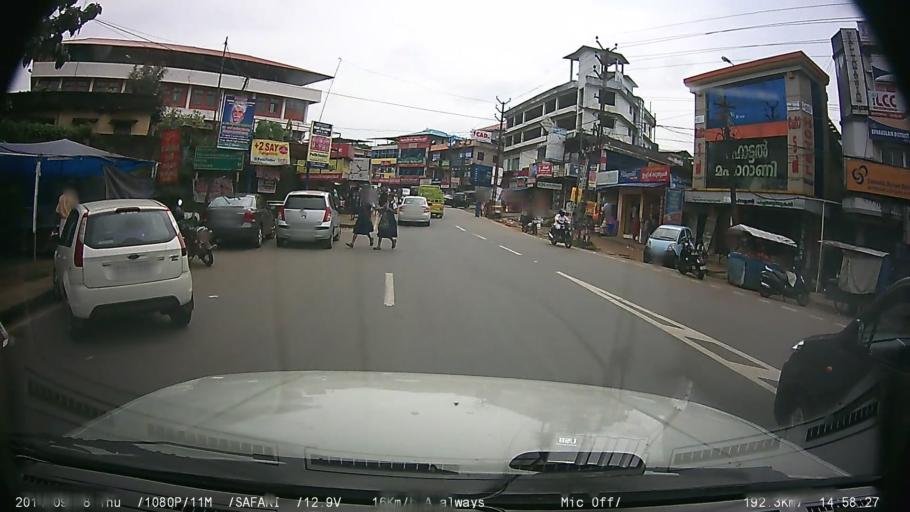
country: IN
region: Kerala
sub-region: Ernakulam
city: Muvattupula
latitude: 9.9801
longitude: 76.5801
